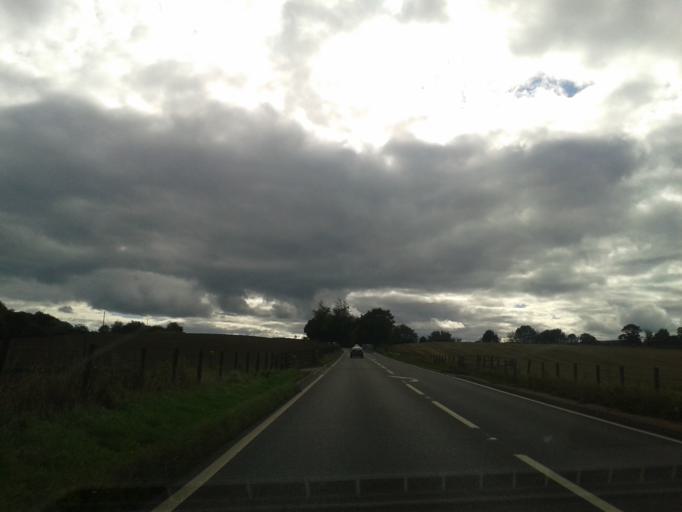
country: GB
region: Scotland
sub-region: Fife
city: Freuchie
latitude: 56.2403
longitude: -3.1545
